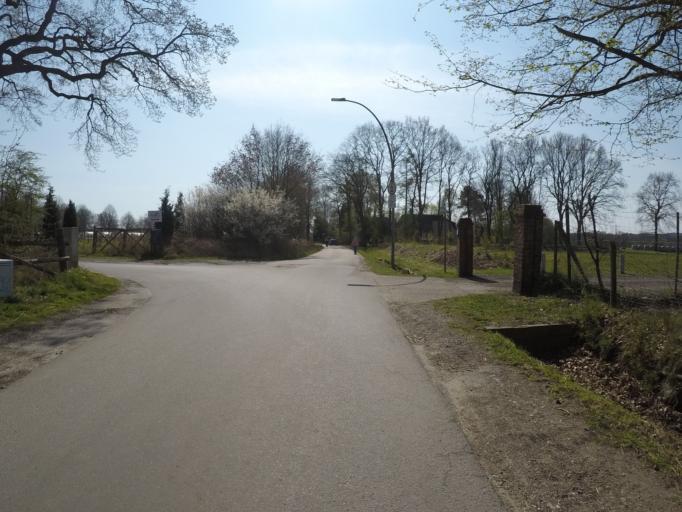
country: DE
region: Schleswig-Holstein
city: Halstenbek
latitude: 53.5913
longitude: 9.8174
